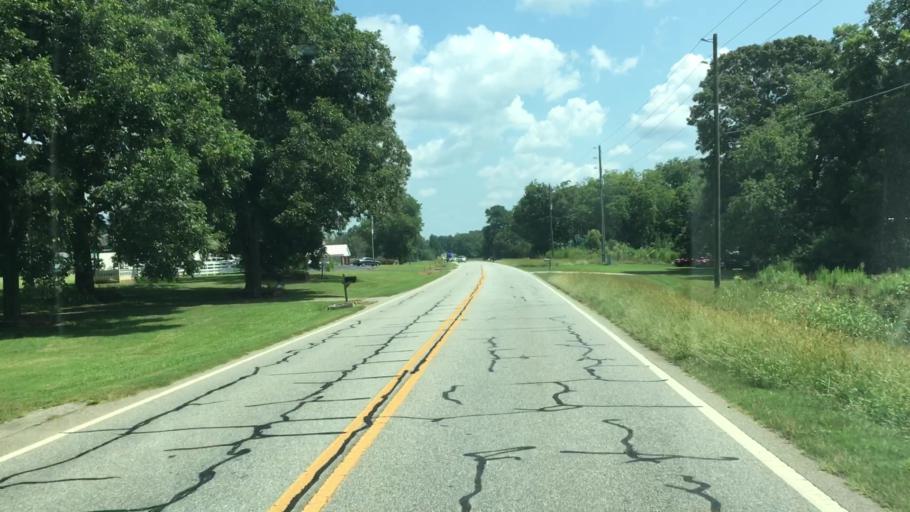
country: US
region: Georgia
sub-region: Barrow County
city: Statham
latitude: 33.9426
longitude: -83.6431
